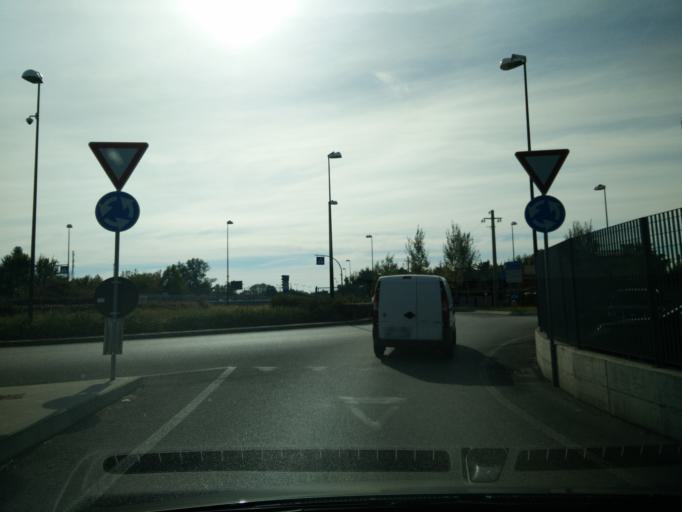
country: IT
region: Veneto
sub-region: Provincia di Venezia
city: Campalto
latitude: 45.4998
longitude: 12.2736
